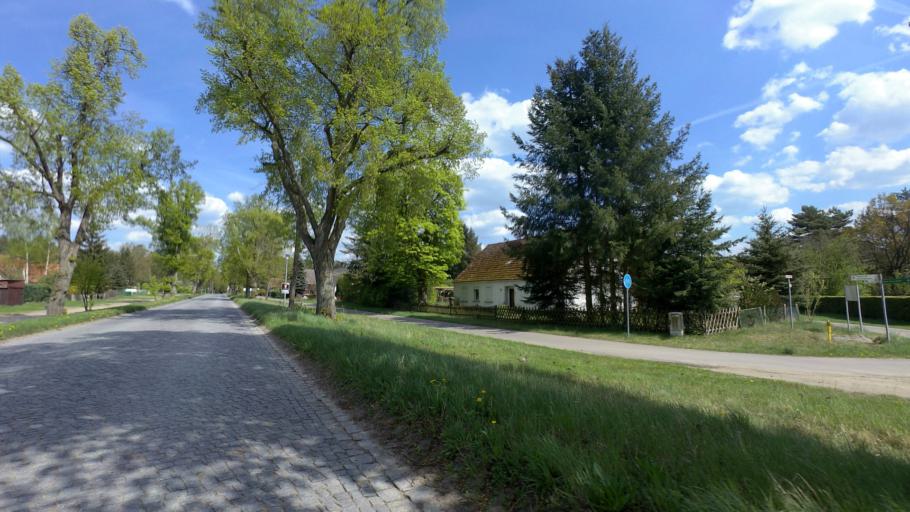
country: DE
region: Brandenburg
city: Milmersdorf
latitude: 53.0514
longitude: 13.6086
